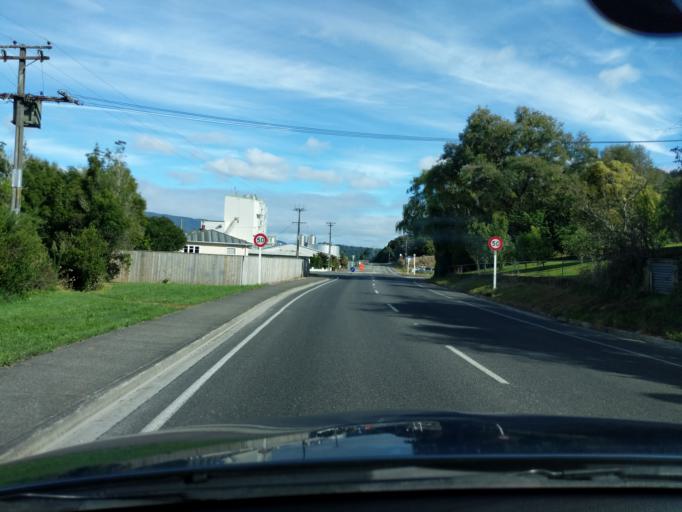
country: NZ
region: Tasman
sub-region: Tasman District
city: Takaka
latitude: -40.8556
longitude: 172.8170
